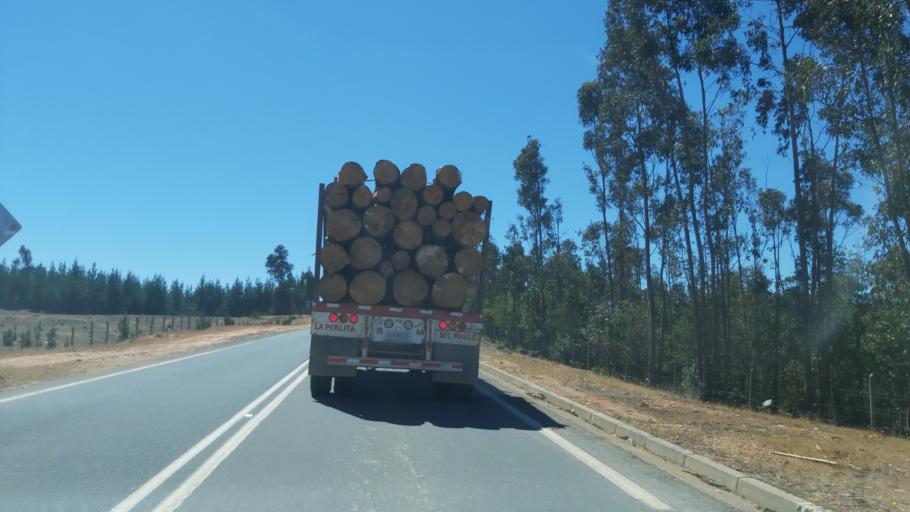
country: CL
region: Maule
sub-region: Provincia de Talca
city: Talca
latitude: -34.9487
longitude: -71.9664
